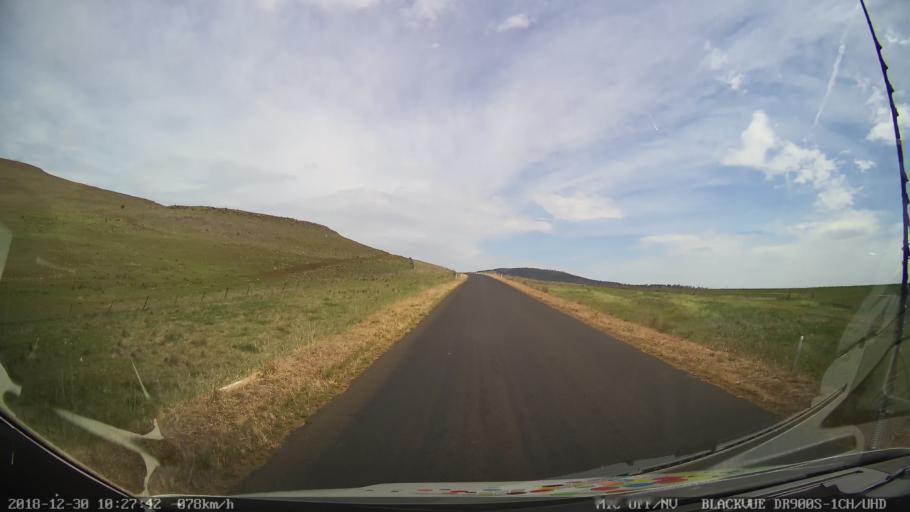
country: AU
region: New South Wales
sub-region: Snowy River
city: Berridale
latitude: -36.5112
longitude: 148.9299
